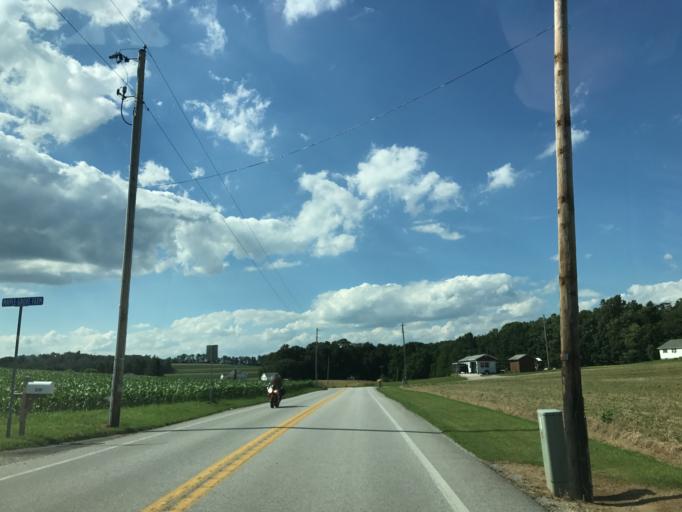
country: US
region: Pennsylvania
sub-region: York County
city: New Freedom
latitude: 39.7334
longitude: -76.7755
